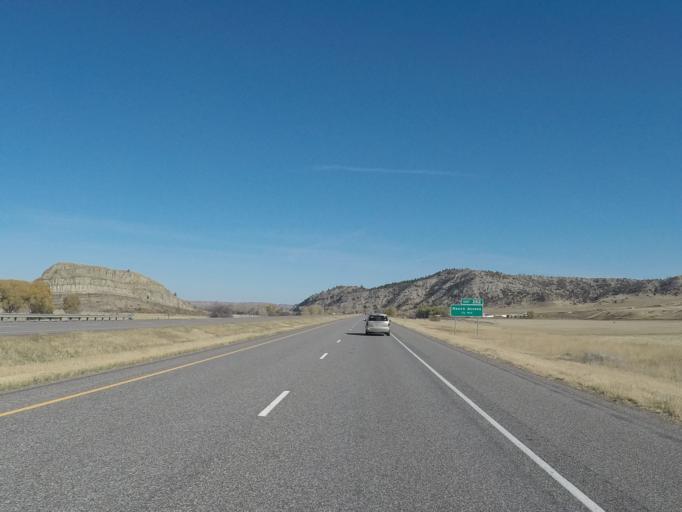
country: US
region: Montana
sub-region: Park County
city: Livingston
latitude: 45.7199
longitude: -110.2536
